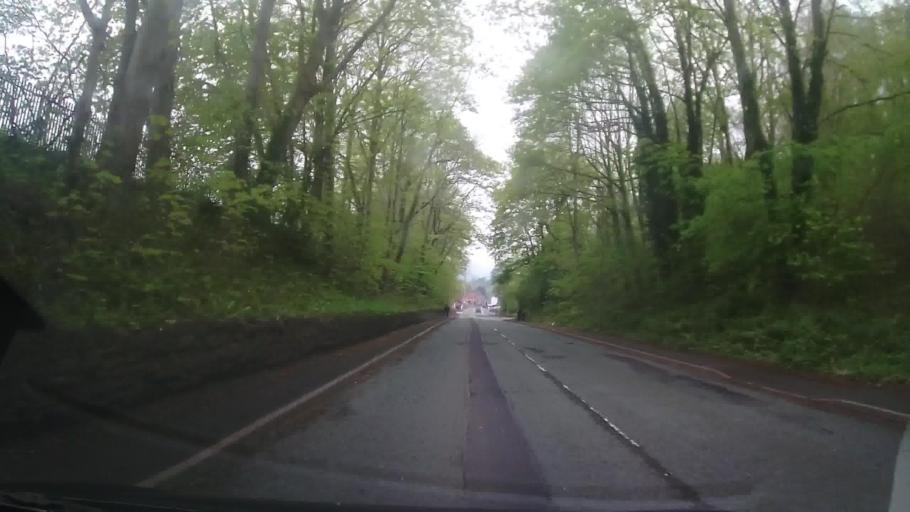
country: GB
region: Wales
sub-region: Wrexham
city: Rhosllanerchrugog
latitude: 52.9812
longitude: -3.0737
